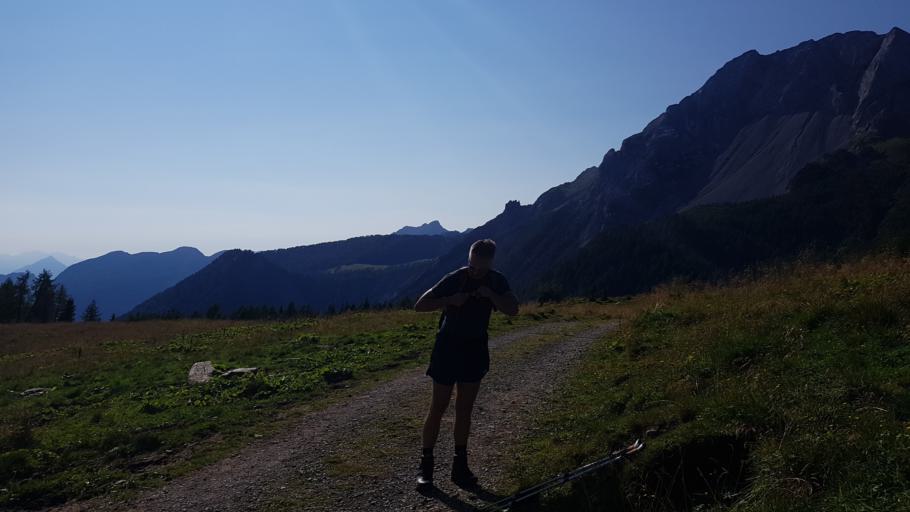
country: IT
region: Friuli Venezia Giulia
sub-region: Provincia di Udine
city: Vico
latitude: 46.4639
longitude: 12.6276
